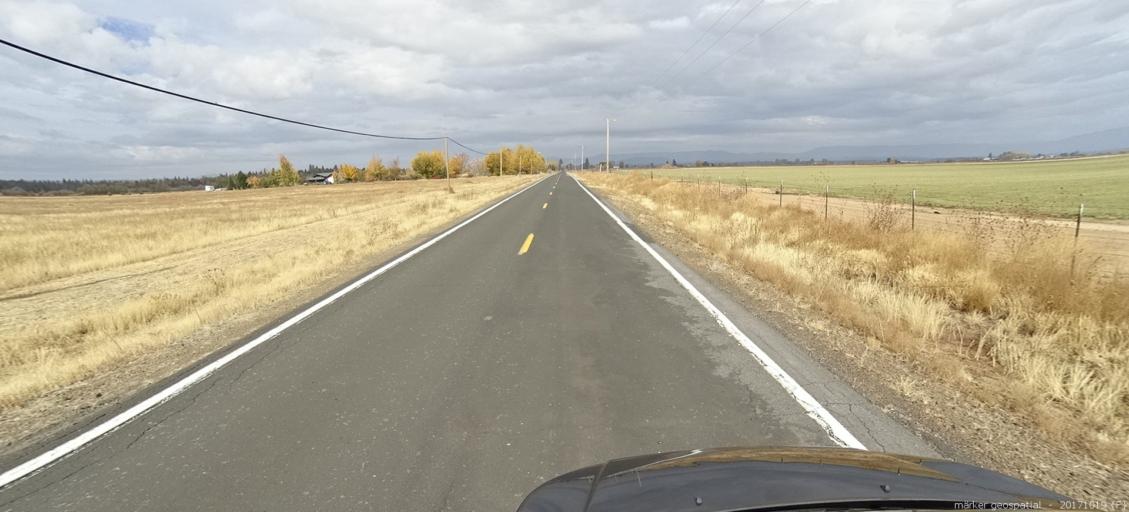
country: US
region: California
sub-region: Shasta County
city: Burney
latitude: 41.0657
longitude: -121.5092
